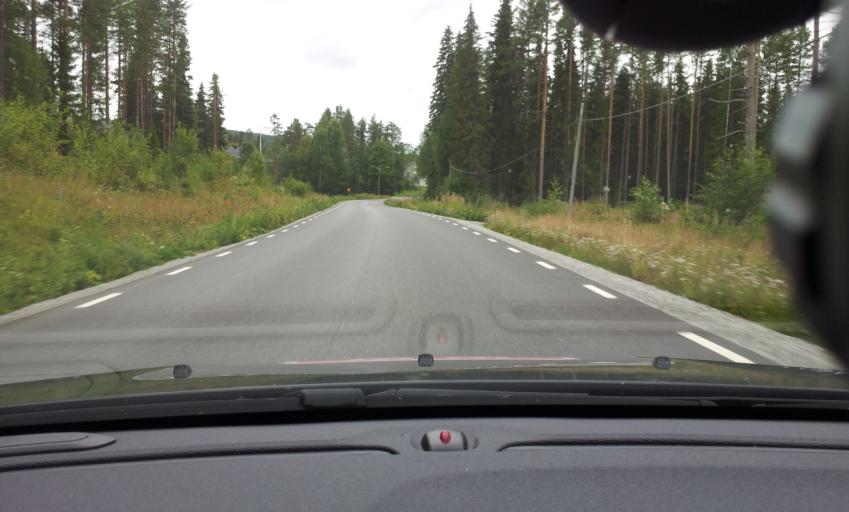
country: SE
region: Jaemtland
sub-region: Braecke Kommun
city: Braecke
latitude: 63.0621
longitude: 15.3431
